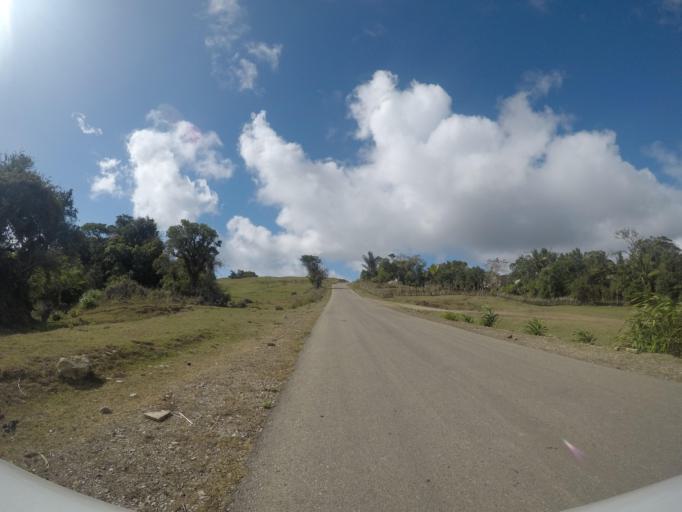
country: TL
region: Lautem
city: Lospalos
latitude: -8.4807
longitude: 126.8693
